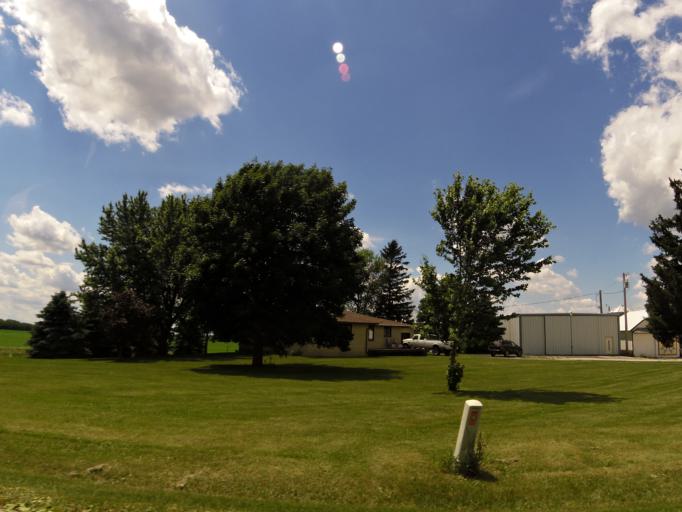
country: US
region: Iowa
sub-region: Buchanan County
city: Independence
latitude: 42.5096
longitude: -91.8898
